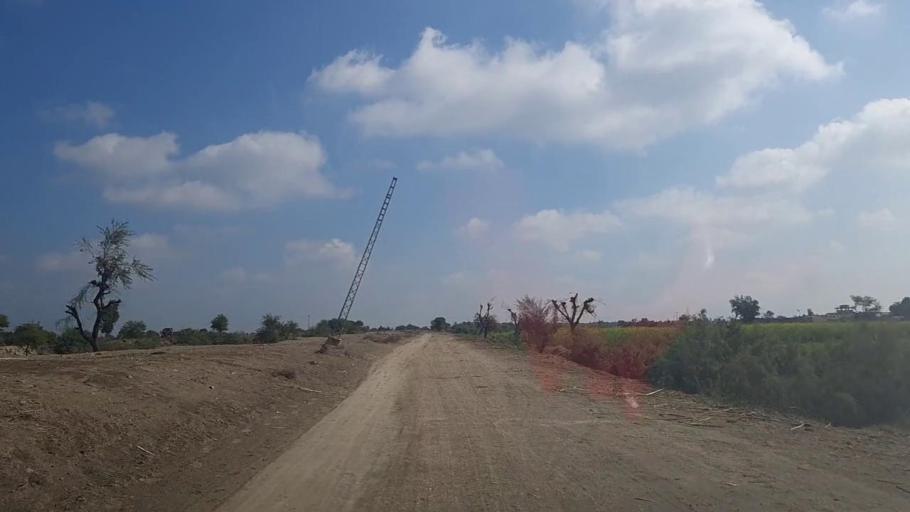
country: PK
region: Sindh
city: Sanghar
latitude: 26.0541
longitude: 68.9713
